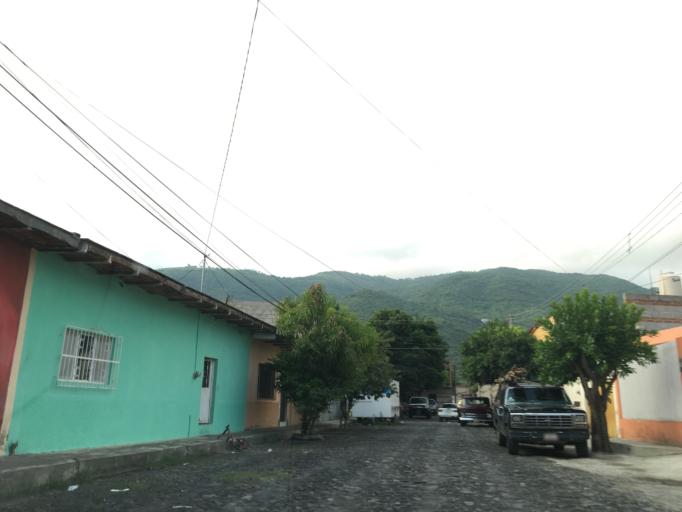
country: MX
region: Nayarit
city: Jala
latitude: 21.1006
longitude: -104.4347
